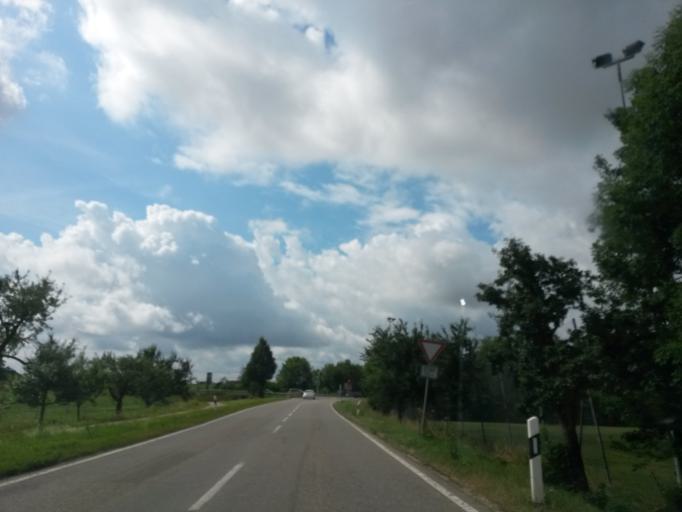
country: DE
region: Baden-Wuerttemberg
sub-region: Regierungsbezirk Stuttgart
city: Ellwangen
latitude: 48.9638
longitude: 10.1635
